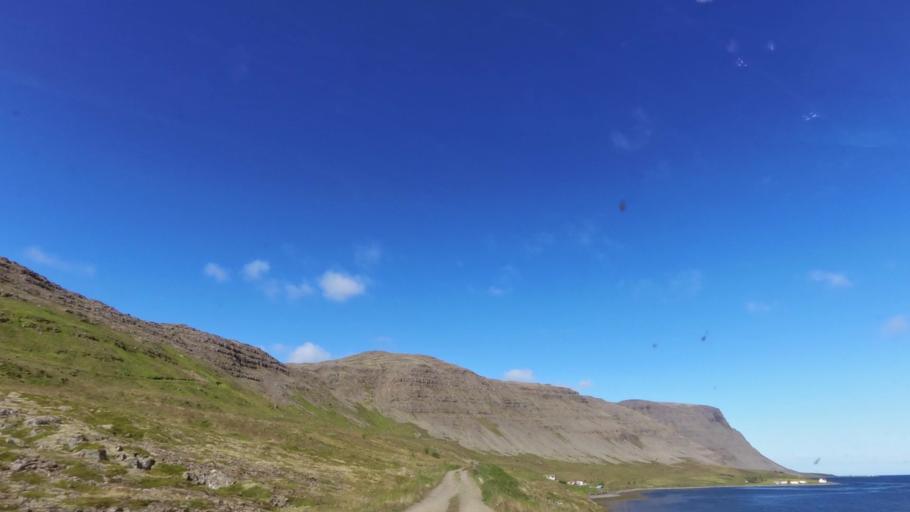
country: IS
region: West
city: Olafsvik
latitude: 65.6170
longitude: -23.8498
